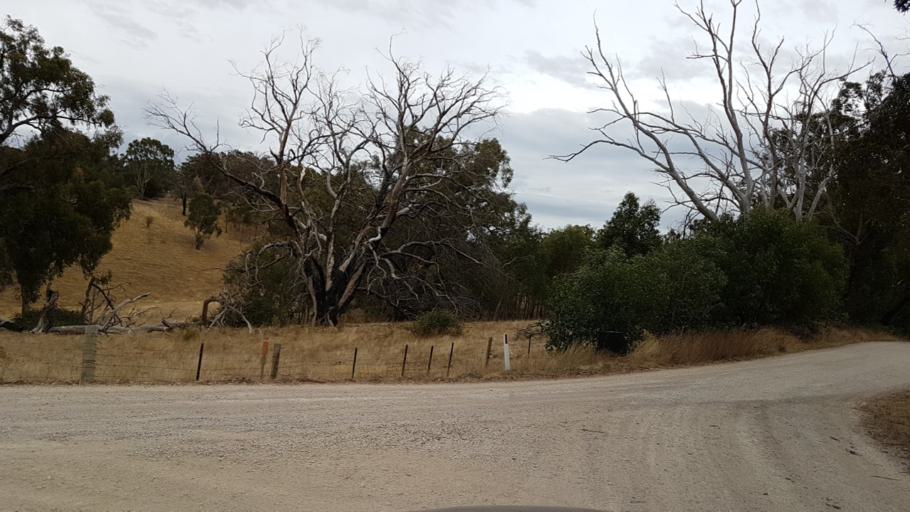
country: AU
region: South Australia
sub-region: Adelaide Hills
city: Gumeracha
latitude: -34.7992
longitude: 138.8171
